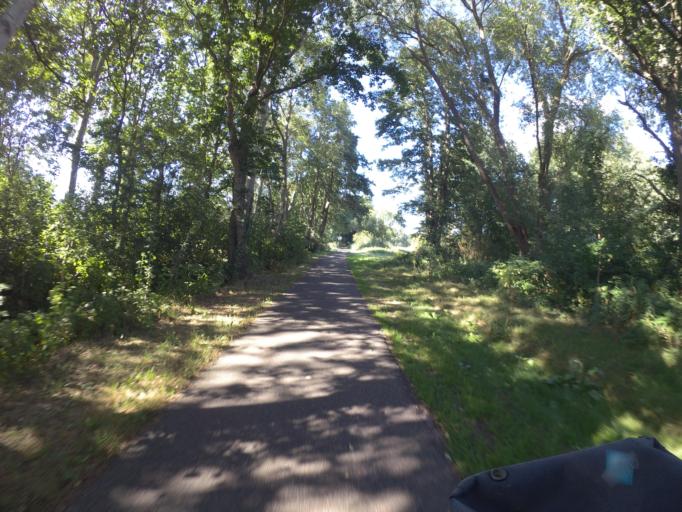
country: NL
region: Drenthe
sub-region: Gemeente Aa en Hunze
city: Anloo
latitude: 52.9980
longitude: 6.6800
